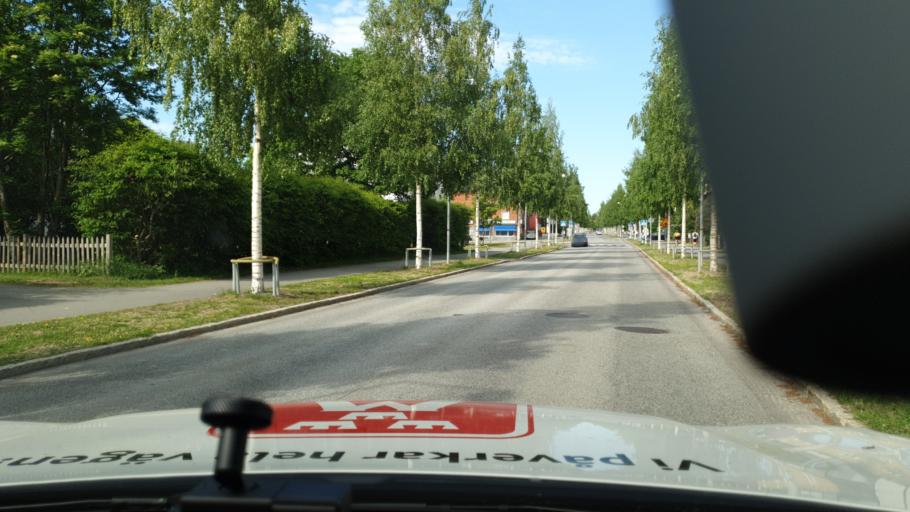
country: SE
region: Vaesterbotten
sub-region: Umea Kommun
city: Umea
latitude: 63.8380
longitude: 20.2833
